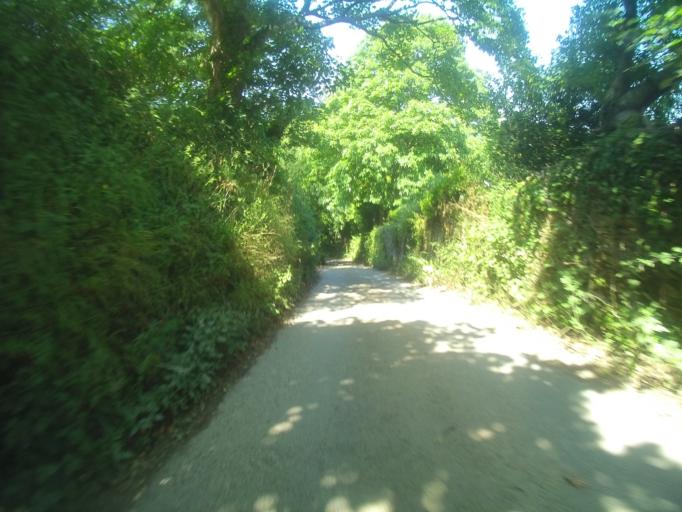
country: GB
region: England
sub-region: Devon
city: Dartmouth
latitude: 50.3551
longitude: -3.5983
